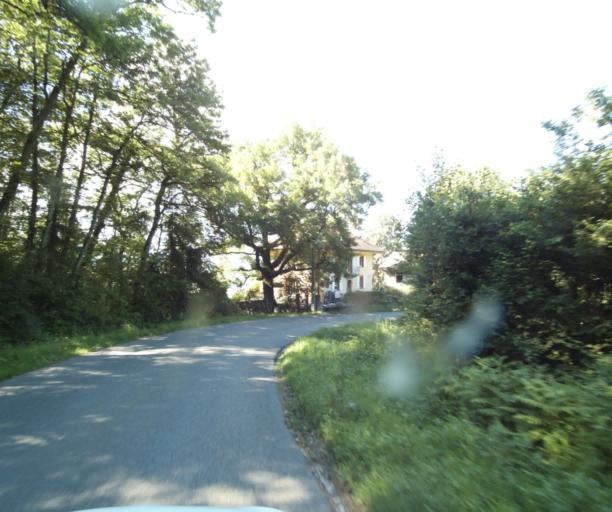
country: FR
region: Rhone-Alpes
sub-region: Departement de la Haute-Savoie
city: Massongy
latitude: 46.3105
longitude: 6.3422
